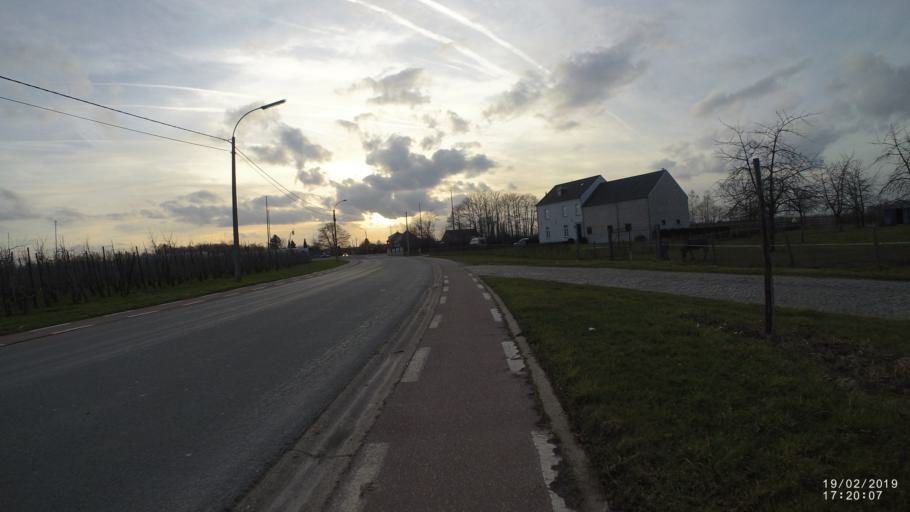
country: BE
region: Flanders
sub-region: Provincie Limburg
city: Sint-Truiden
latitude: 50.8230
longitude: 5.2358
